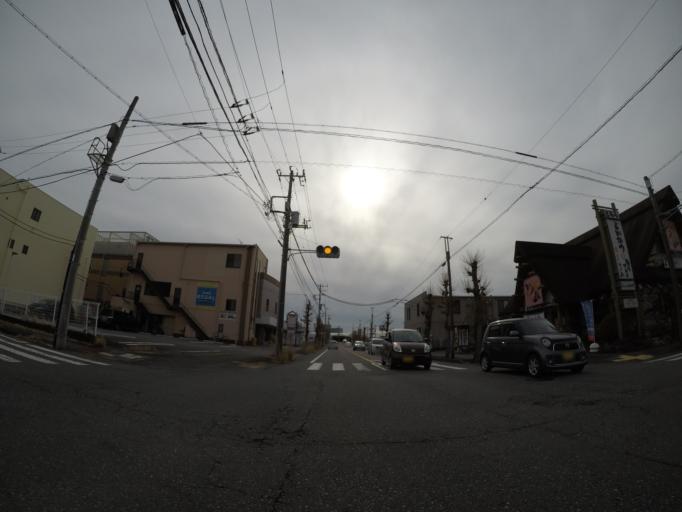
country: JP
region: Shizuoka
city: Fuji
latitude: 35.1532
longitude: 138.6830
